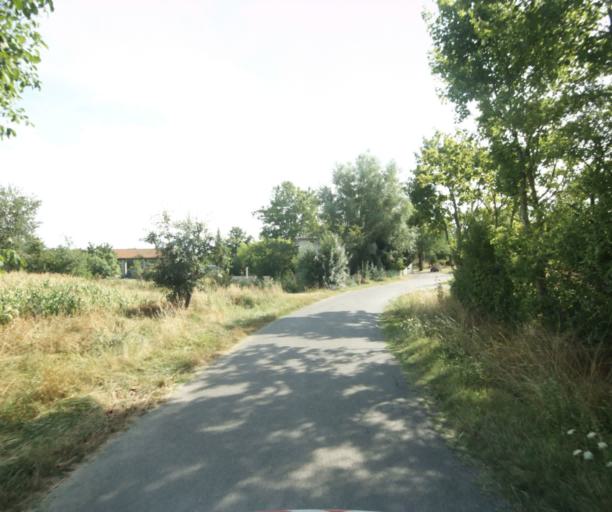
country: FR
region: Midi-Pyrenees
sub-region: Departement du Tarn
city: Puylaurens
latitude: 43.5258
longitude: 2.0026
